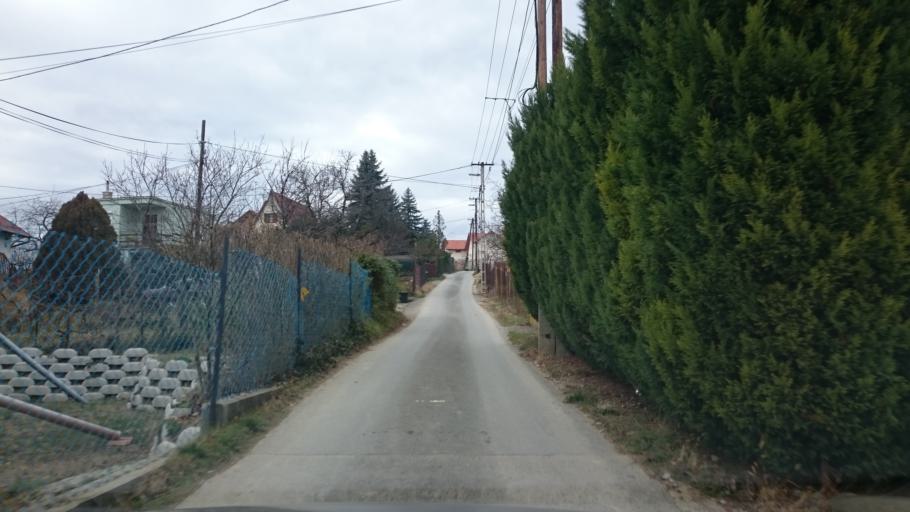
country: HU
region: Baranya
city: Pellerd
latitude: 46.0700
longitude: 18.1813
